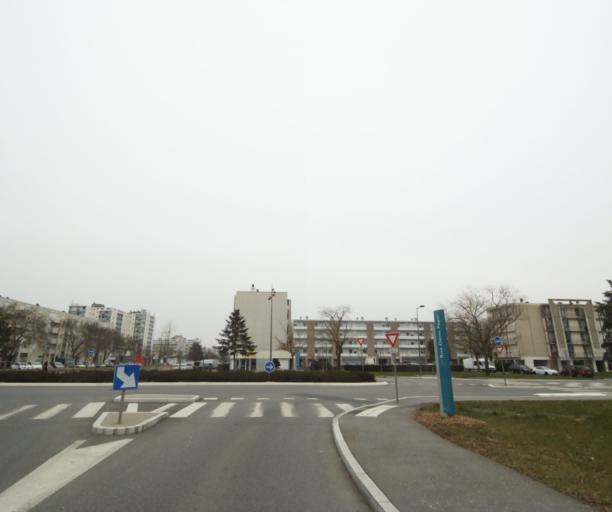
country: FR
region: Poitou-Charentes
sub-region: Departement des Deux-Sevres
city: Niort
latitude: 46.3131
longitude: -0.4816
